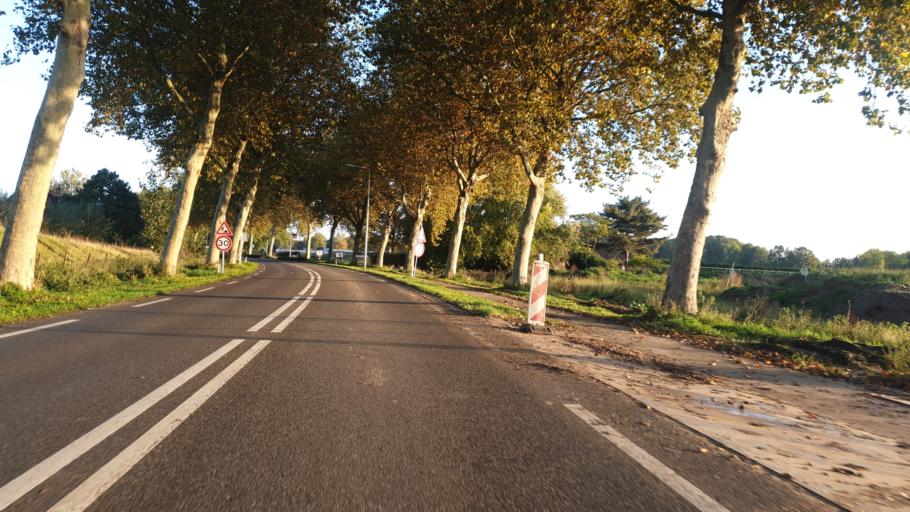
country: NL
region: Gelderland
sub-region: Gemeente Druten
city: Druten
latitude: 51.8785
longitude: 5.6106
